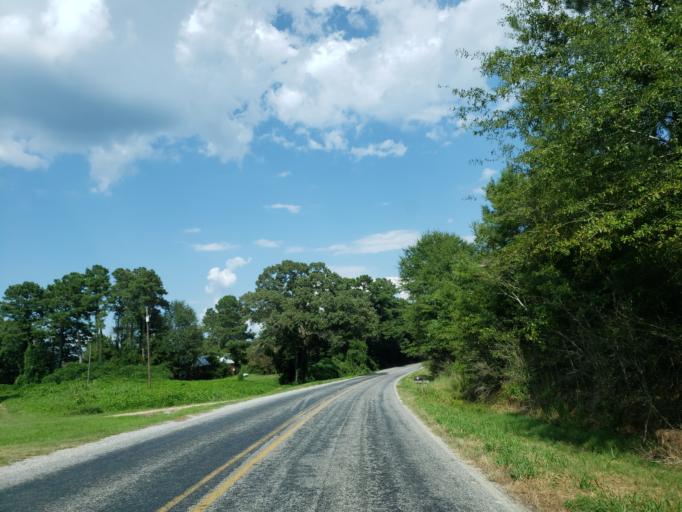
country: US
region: Mississippi
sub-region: Covington County
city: Collins
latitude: 31.6197
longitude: -89.3841
